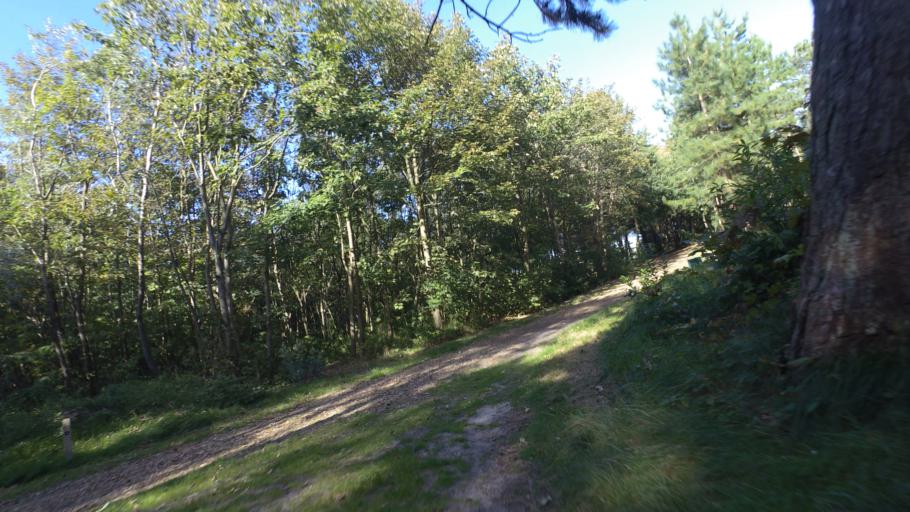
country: NL
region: Friesland
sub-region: Gemeente Ameland
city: Nes
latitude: 53.4542
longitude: 5.7649
